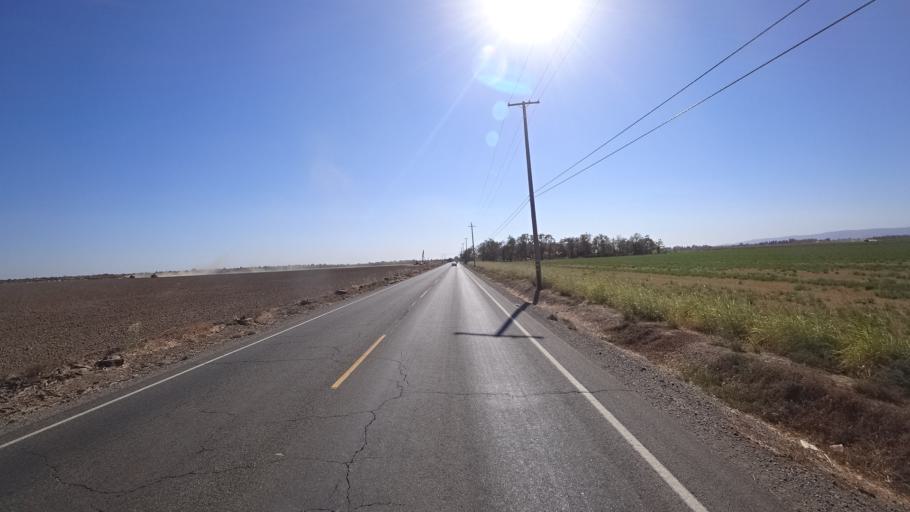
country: US
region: California
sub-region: Yolo County
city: Davis
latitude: 38.5713
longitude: -121.8033
